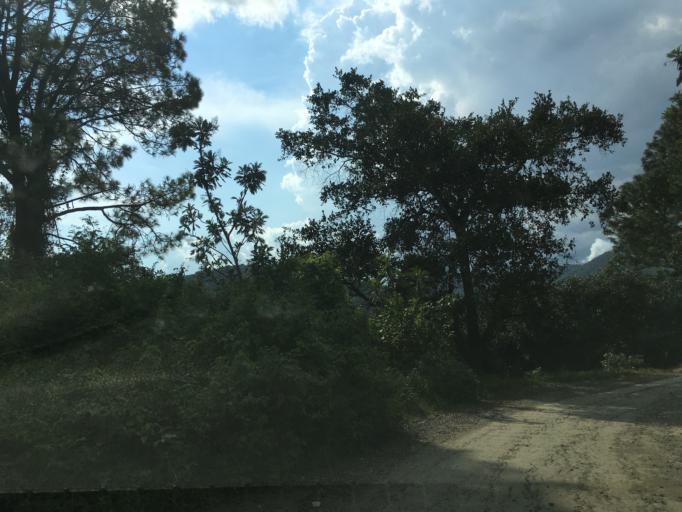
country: MX
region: Michoacan
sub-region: Ziracuaretiro
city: Patuan
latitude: 19.4419
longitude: -101.8820
